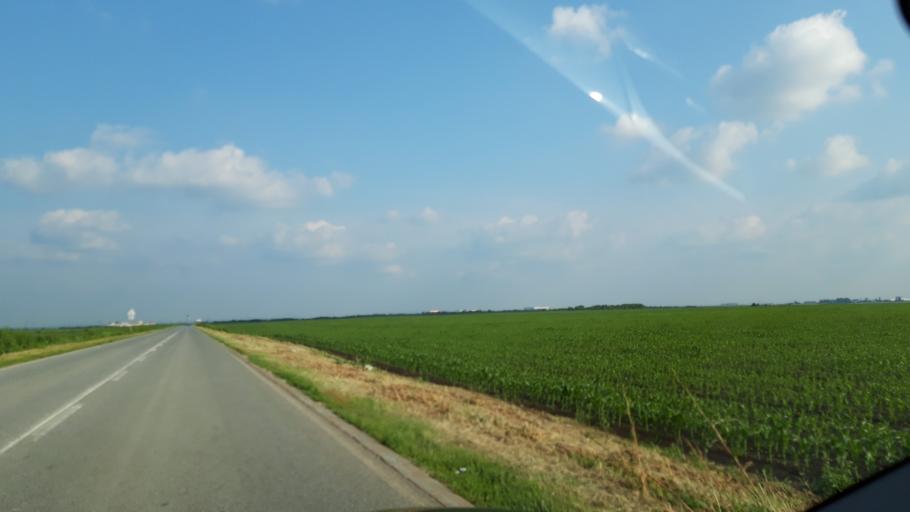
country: RS
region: Autonomna Pokrajina Vojvodina
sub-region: Sremski Okrug
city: Ingija
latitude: 45.0860
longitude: 20.1107
